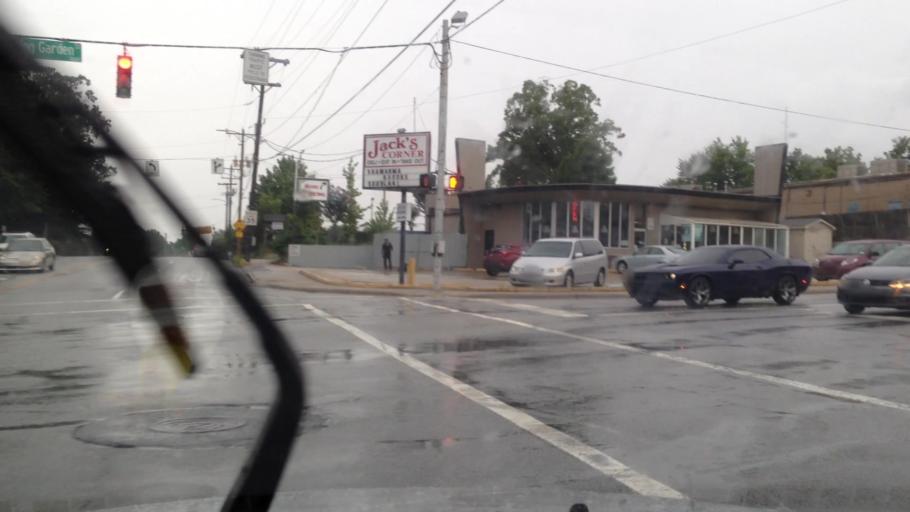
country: US
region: North Carolina
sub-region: Guilford County
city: Greensboro
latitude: 36.0648
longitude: -79.8154
